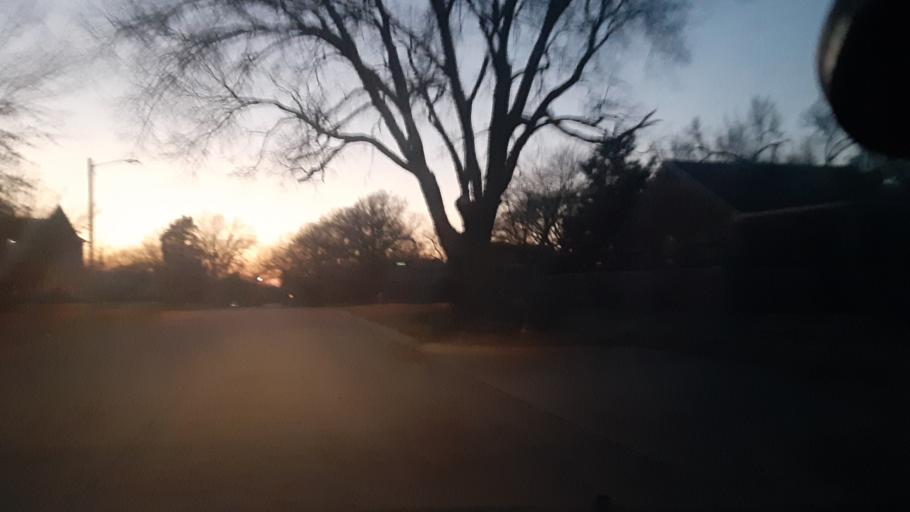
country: US
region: Oklahoma
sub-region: Payne County
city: Stillwater
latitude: 36.1113
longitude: -97.0635
